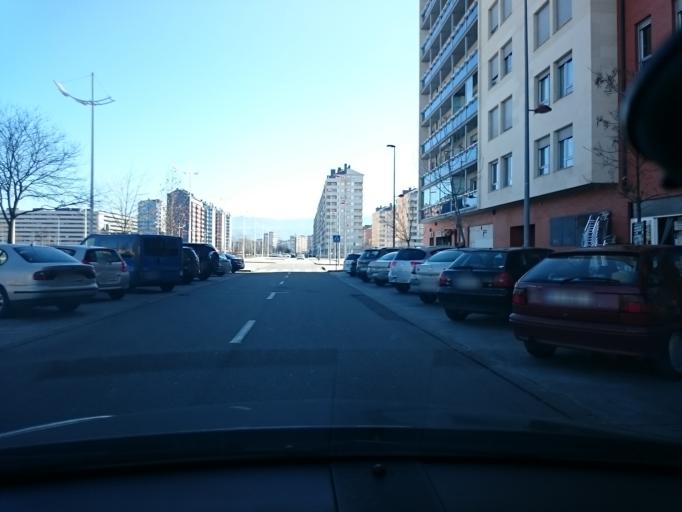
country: ES
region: Castille and Leon
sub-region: Provincia de Leon
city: Ponferrada
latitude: 42.5564
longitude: -6.6079
